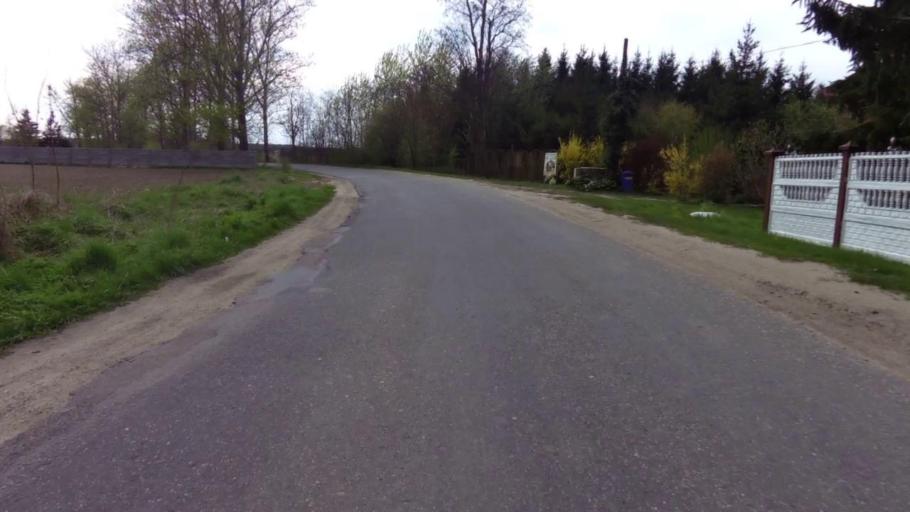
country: PL
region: West Pomeranian Voivodeship
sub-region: Powiat kamienski
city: Wolin
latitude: 53.9650
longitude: 14.6218
